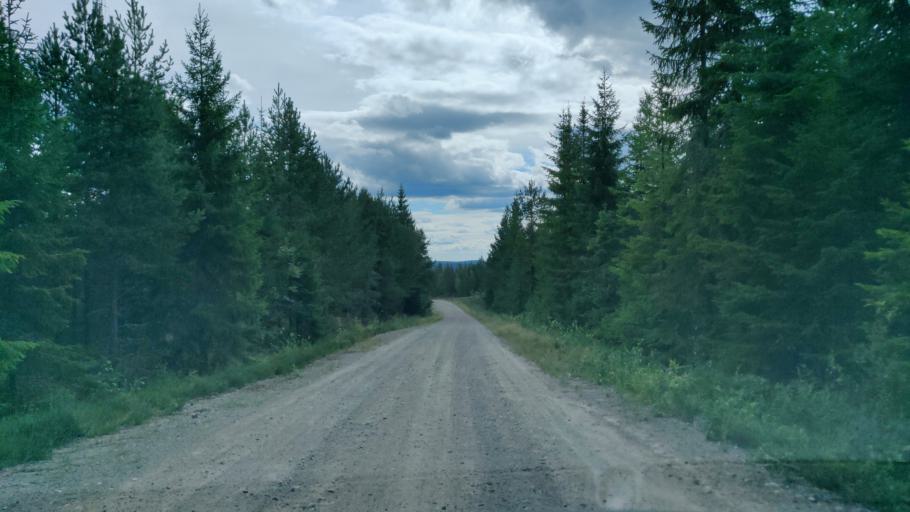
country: SE
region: Vaermland
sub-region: Hagfors Kommun
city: Hagfors
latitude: 60.0166
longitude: 13.7301
